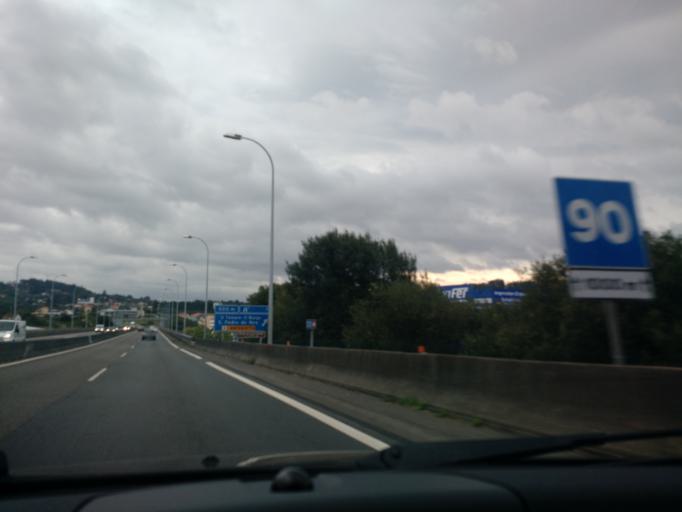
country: ES
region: Galicia
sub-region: Provincia da Coruna
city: Cambre
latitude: 43.3120
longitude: -8.3607
